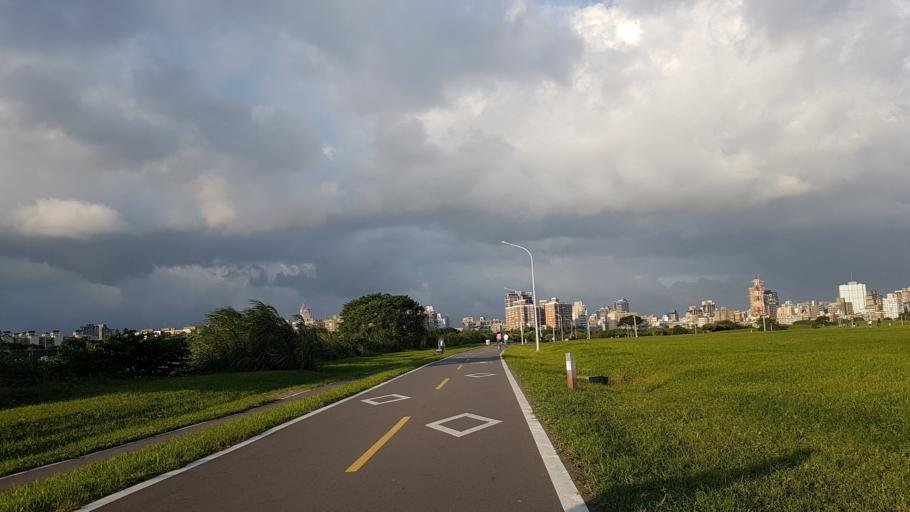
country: TW
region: Taipei
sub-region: Taipei
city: Banqiao
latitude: 25.0173
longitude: 121.5060
